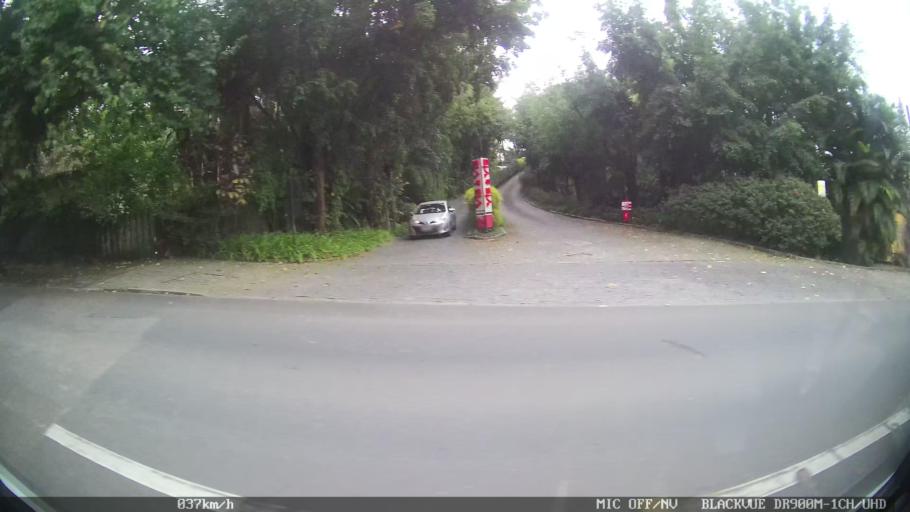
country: BR
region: Santa Catarina
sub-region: Joinville
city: Joinville
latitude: -26.2960
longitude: -48.8602
